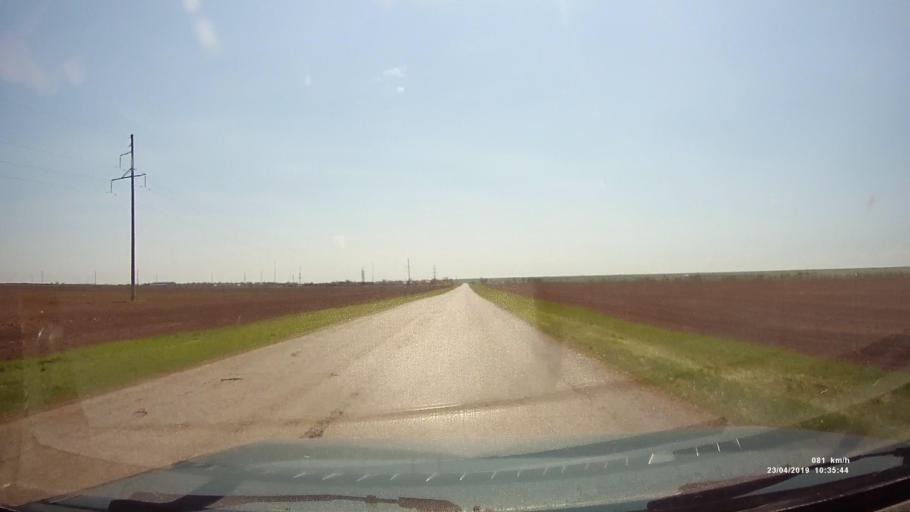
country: RU
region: Kalmykiya
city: Yashalta
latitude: 46.5511
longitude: 42.6279
